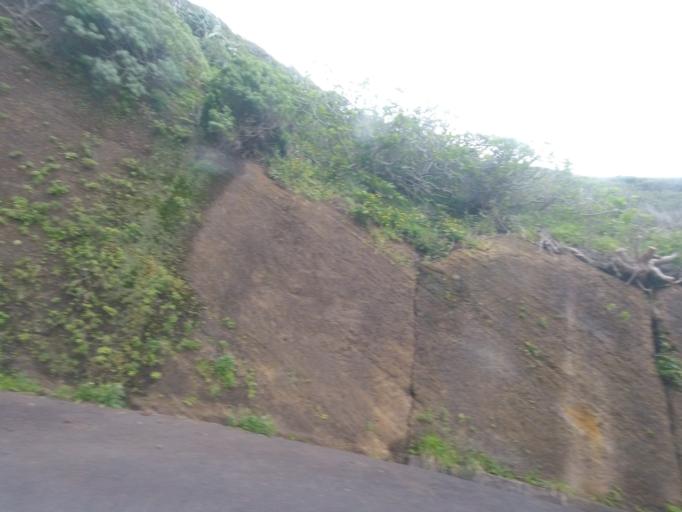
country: PT
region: Madeira
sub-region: Porto Moniz
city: Porto Moniz
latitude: 32.8545
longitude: -17.1556
